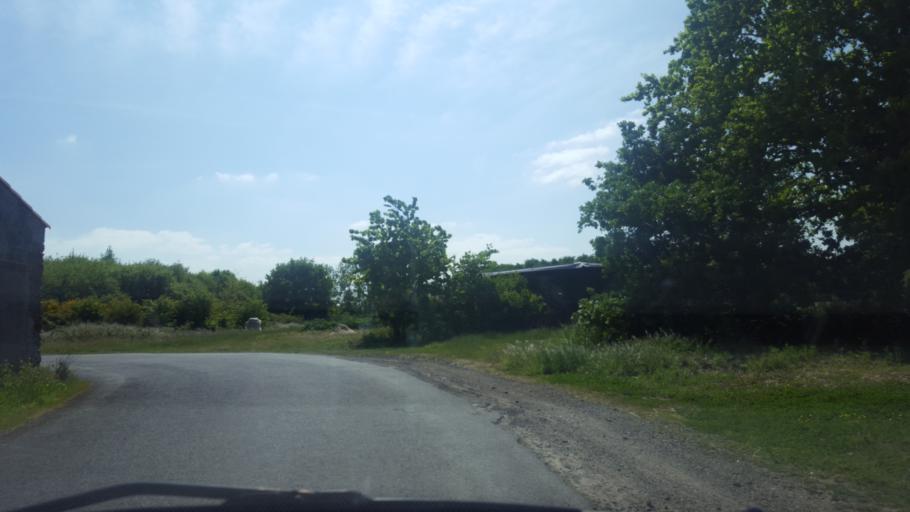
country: FR
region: Pays de la Loire
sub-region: Departement de la Loire-Atlantique
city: La Limouziniere
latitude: 47.0383
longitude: -1.5843
